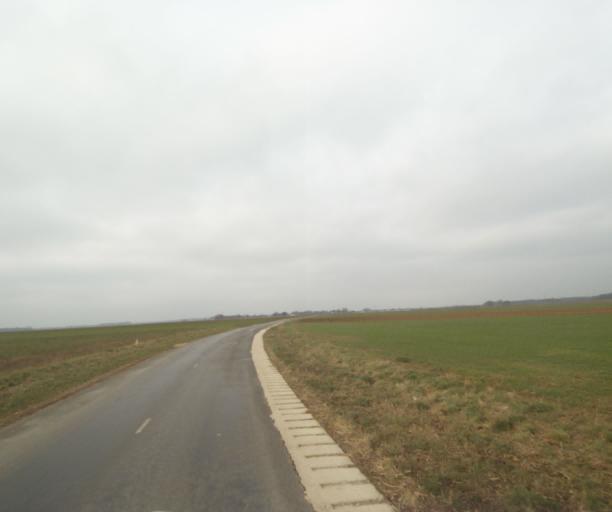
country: FR
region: Champagne-Ardenne
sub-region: Departement de la Haute-Marne
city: Villiers-en-Lieu
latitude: 48.6773
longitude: 4.8565
